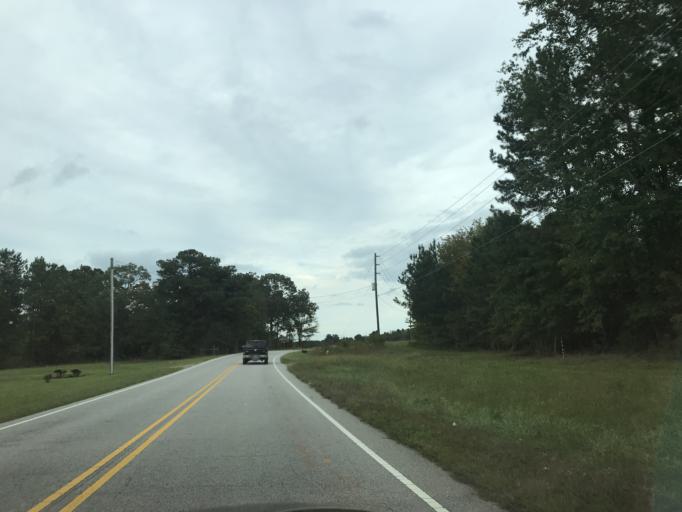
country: US
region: North Carolina
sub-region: Wake County
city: Rolesville
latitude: 35.9832
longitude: -78.3871
